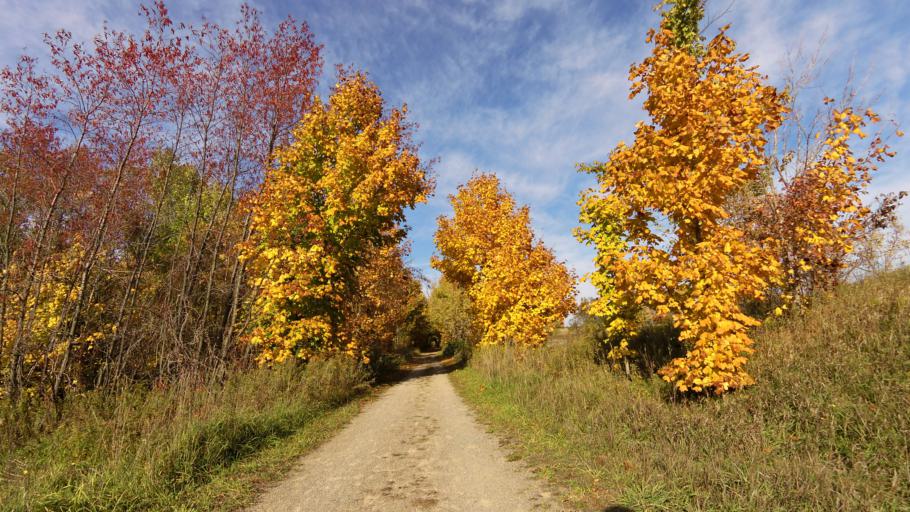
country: CA
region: Ontario
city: Orangeville
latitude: 43.8038
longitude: -80.0346
